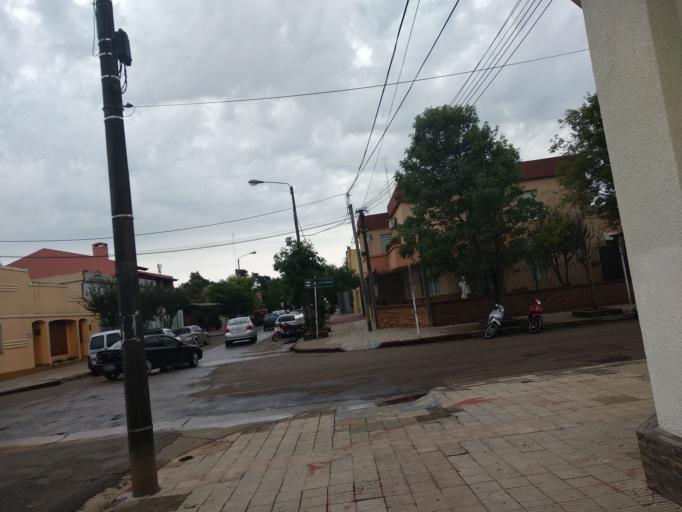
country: UY
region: Artigas
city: Artigas
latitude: -30.4059
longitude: -56.4694
